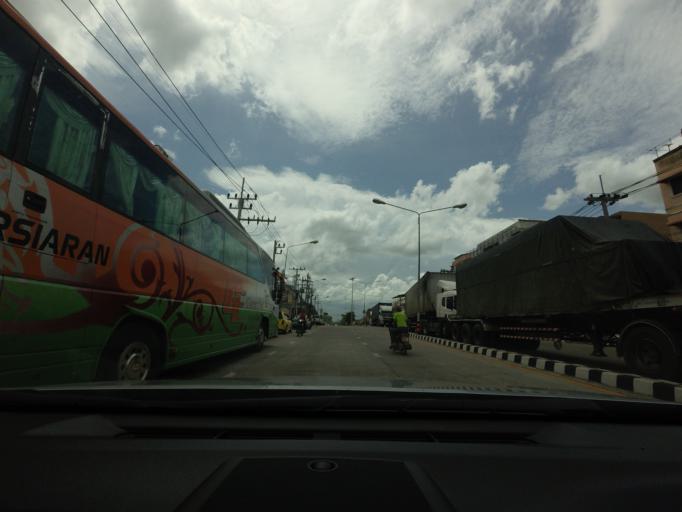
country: TH
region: Songkhla
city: Sadao
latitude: 6.5231
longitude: 100.4186
